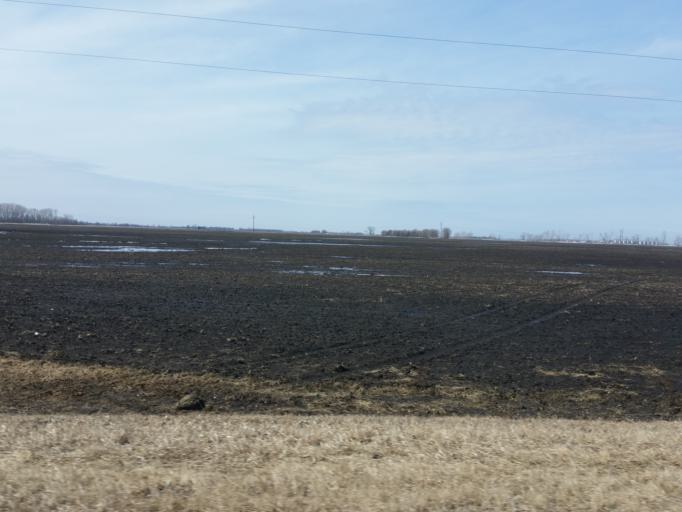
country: US
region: North Dakota
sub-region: Walsh County
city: Grafton
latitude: 48.2835
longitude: -97.2546
